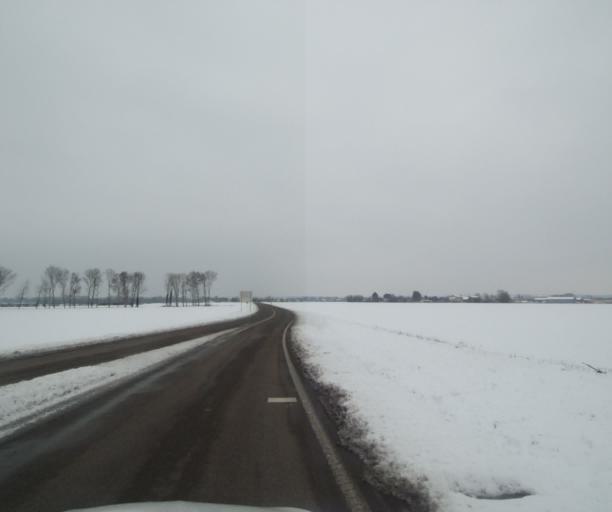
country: FR
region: Champagne-Ardenne
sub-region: Departement de la Haute-Marne
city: Saint-Dizier
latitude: 48.6206
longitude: 4.9278
